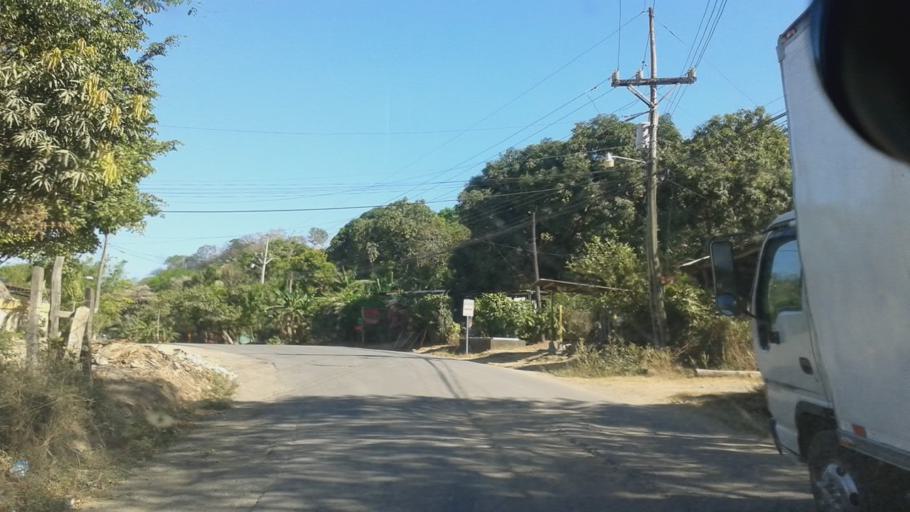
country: CR
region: Guanacaste
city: Samara
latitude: 9.9065
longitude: -85.5956
